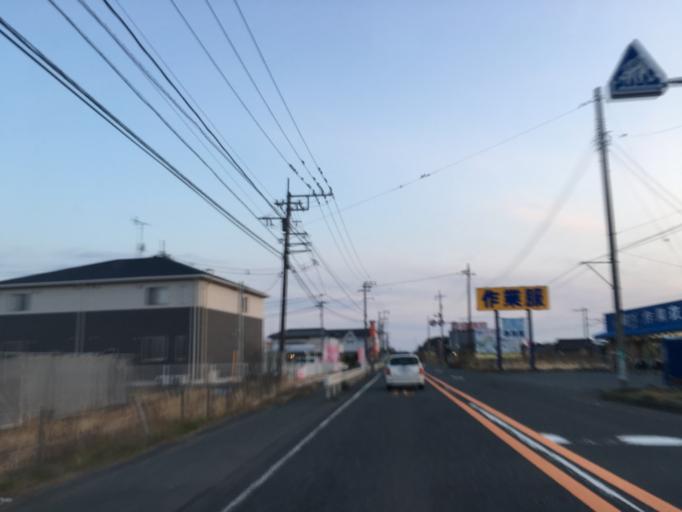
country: JP
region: Ibaraki
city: Kitaibaraki
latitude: 36.7753
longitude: 140.7400
